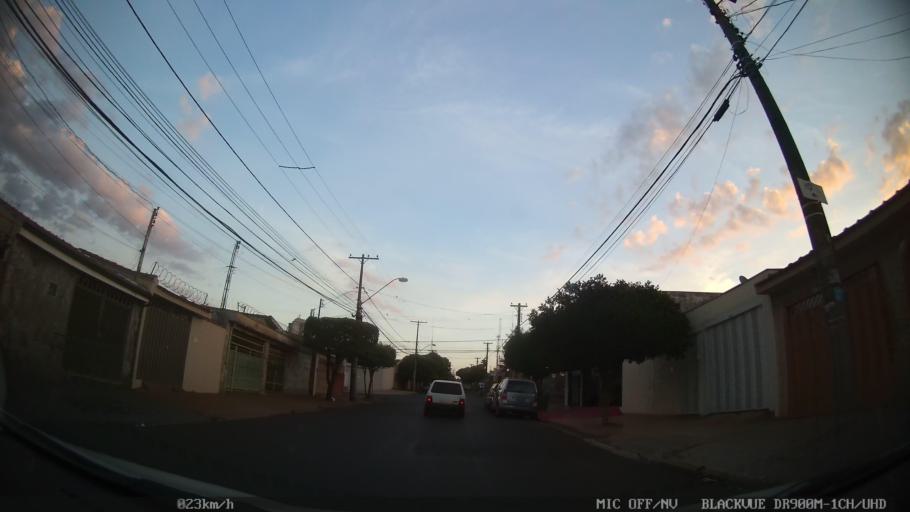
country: BR
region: Sao Paulo
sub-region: Ribeirao Preto
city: Ribeirao Preto
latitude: -21.1509
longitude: -47.8268
